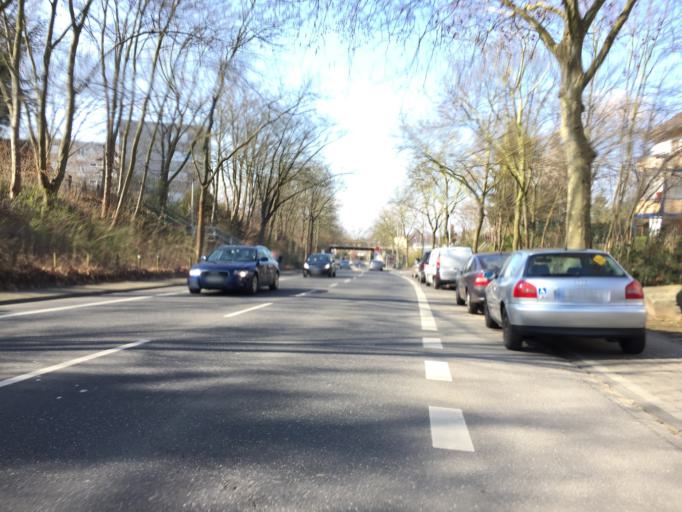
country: DE
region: North Rhine-Westphalia
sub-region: Regierungsbezirk Koln
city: Bonn
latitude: 50.7343
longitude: 7.0635
